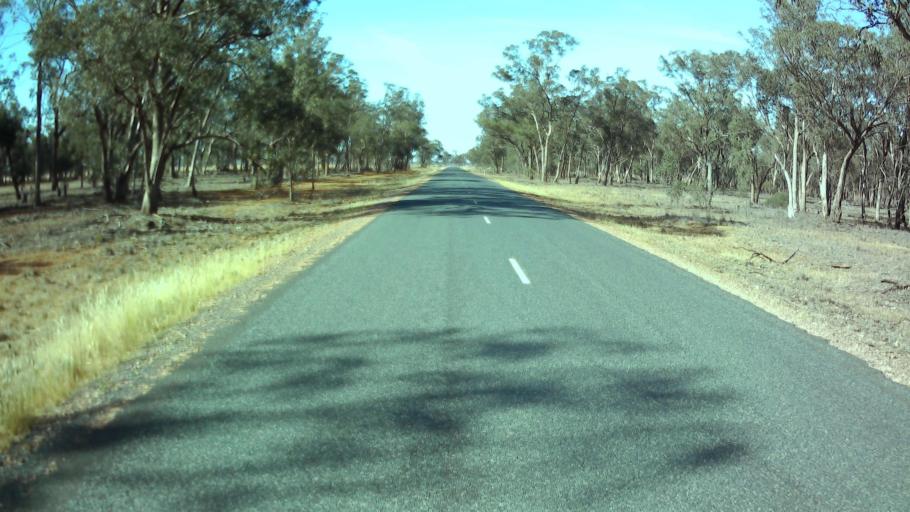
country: AU
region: New South Wales
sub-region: Weddin
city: Grenfell
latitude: -34.0649
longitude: 147.9075
